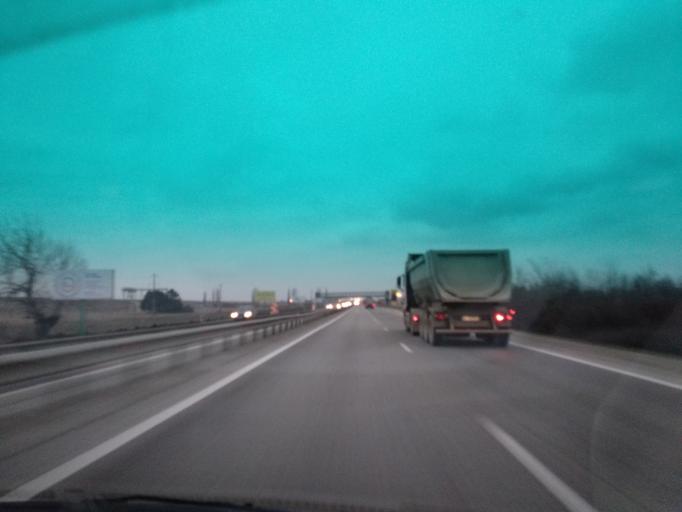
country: RU
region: Adygeya
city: Adygeysk
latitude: 44.9160
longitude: 39.1490
